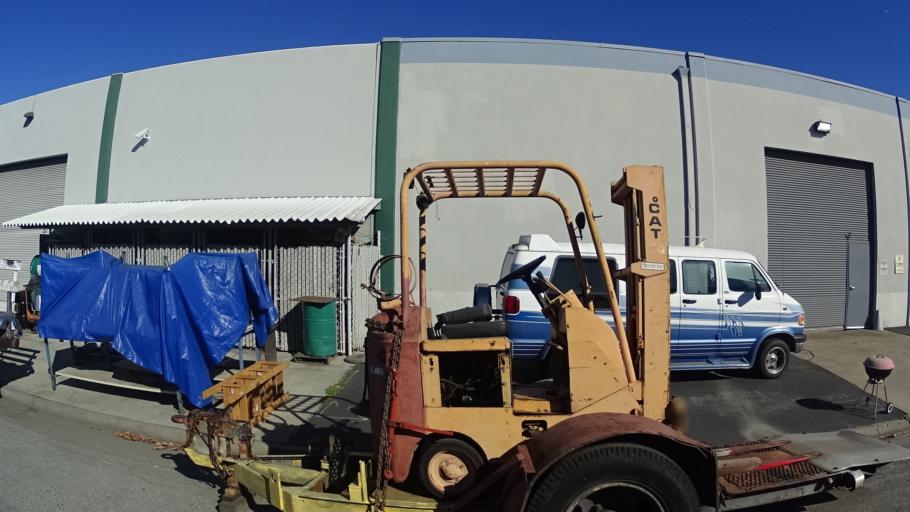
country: US
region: California
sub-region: Santa Clara County
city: San Jose
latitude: 37.3677
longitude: -121.9057
